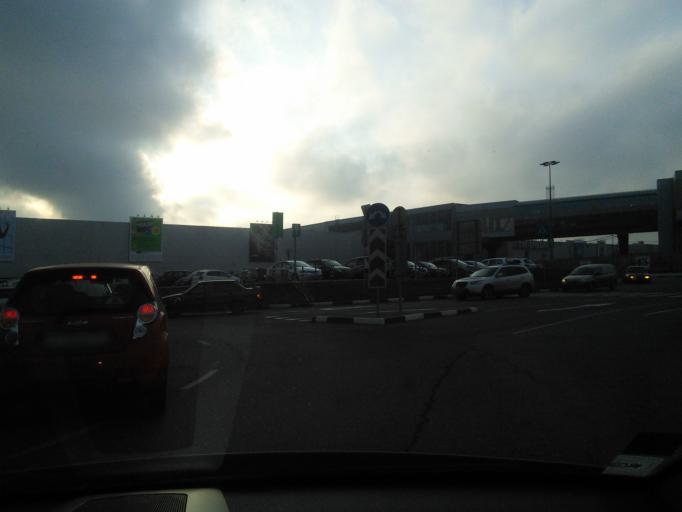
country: RU
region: Moskovskaya
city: Kotel'niki
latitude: 55.6556
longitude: 37.8476
